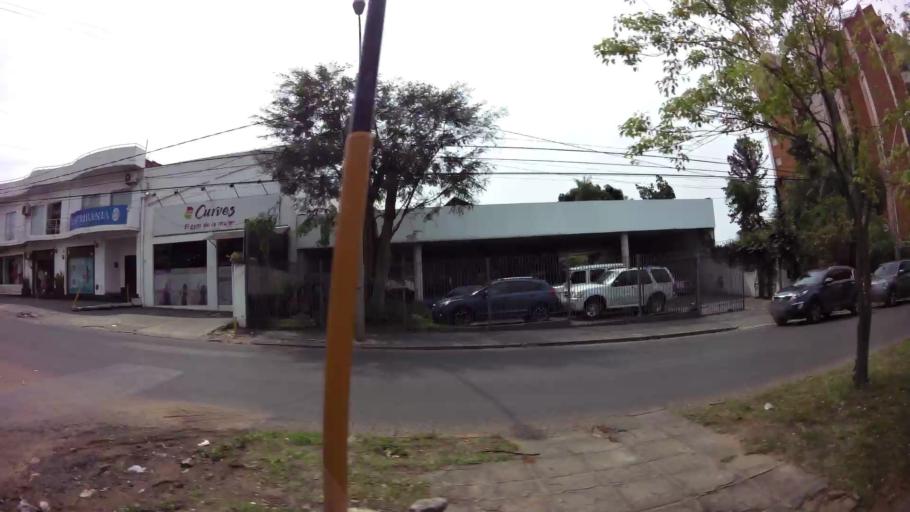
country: PY
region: Asuncion
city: Asuncion
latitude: -25.2767
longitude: -57.5681
